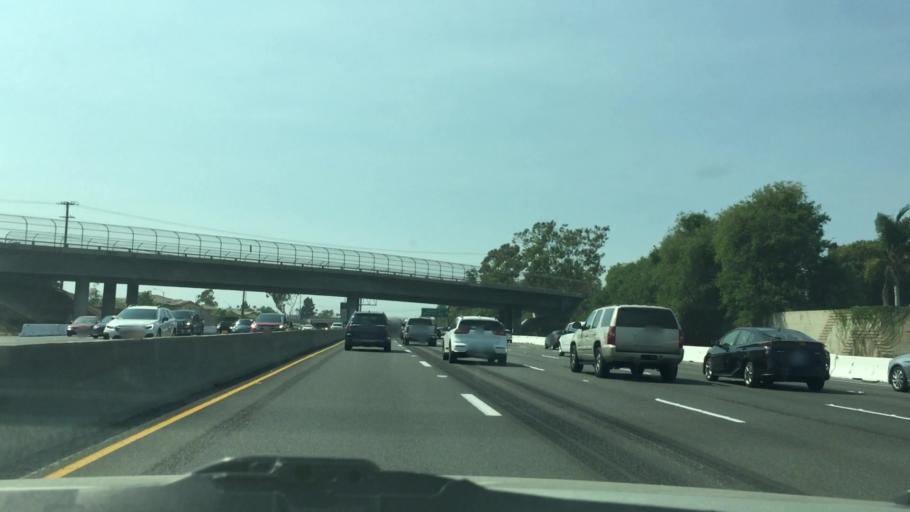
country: US
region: California
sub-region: Orange County
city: Fountain Valley
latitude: 33.7123
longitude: -117.9619
